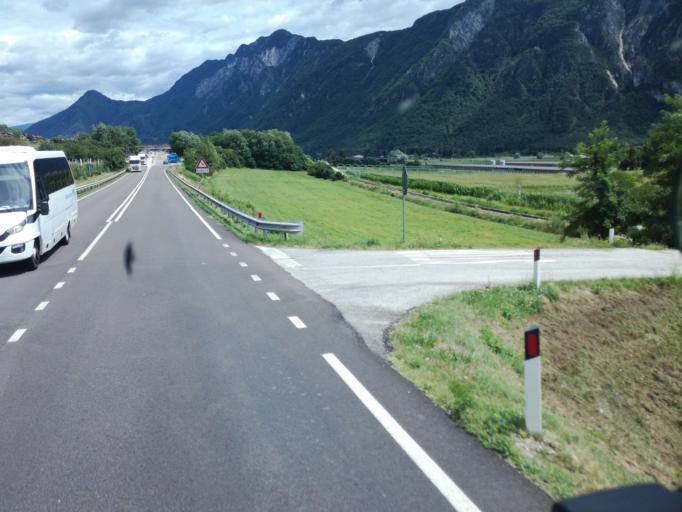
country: IT
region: Trentino-Alto Adige
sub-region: Provincia di Trento
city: Novaledo
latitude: 46.0172
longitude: 11.3428
